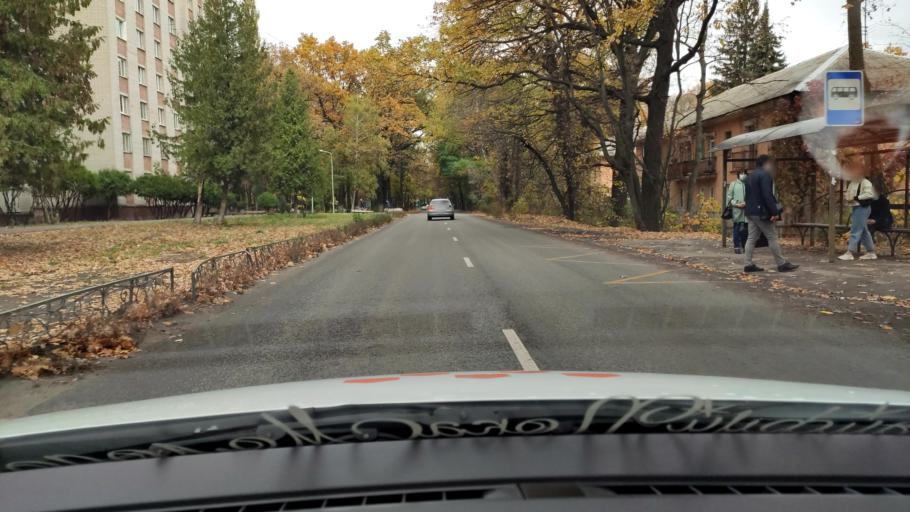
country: RU
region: Voronezj
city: Voronezh
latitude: 51.7204
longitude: 39.2234
